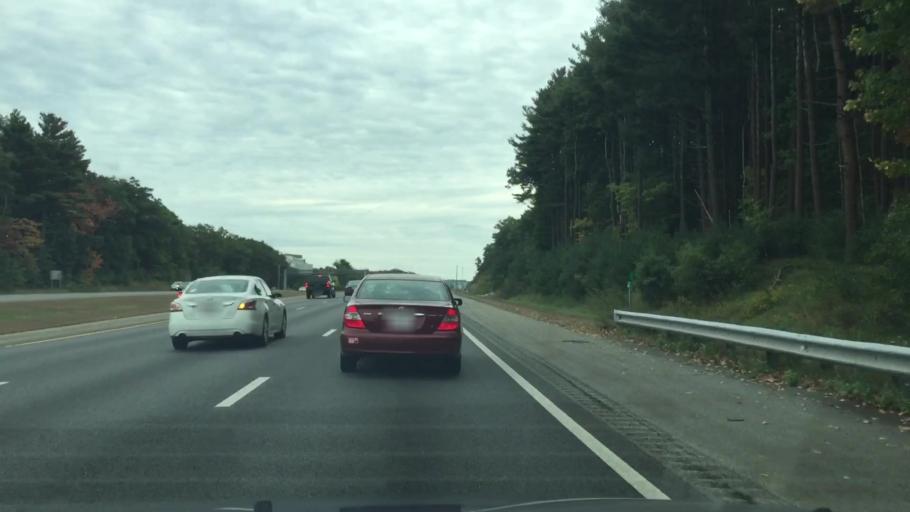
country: US
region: Massachusetts
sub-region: Middlesex County
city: Burlington
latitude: 42.4879
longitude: -71.2294
